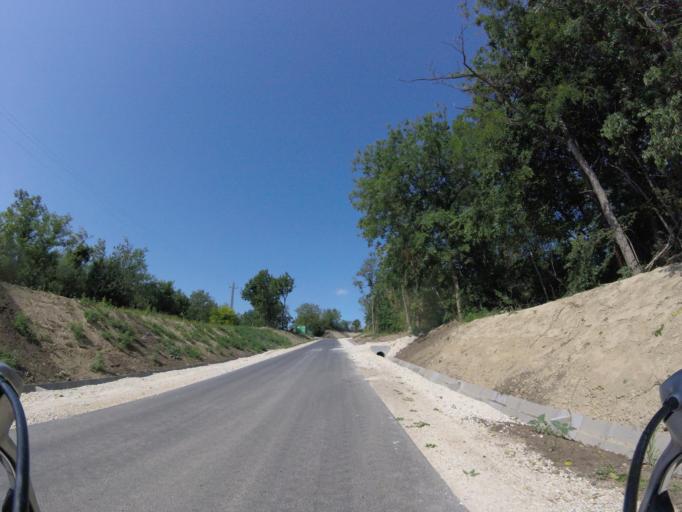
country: HU
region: Fejer
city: Etyek
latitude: 47.4328
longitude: 18.7428
